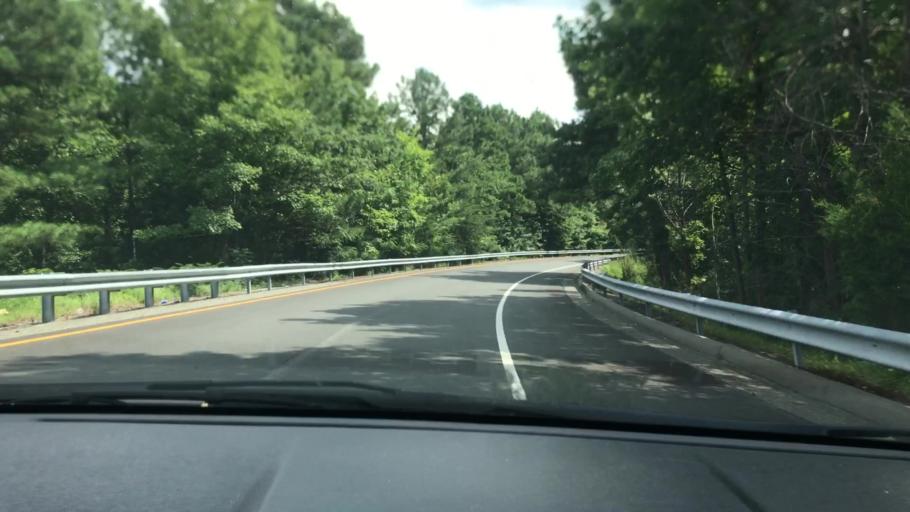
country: US
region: Virginia
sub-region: Henrico County
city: Short Pump
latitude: 37.6361
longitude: -77.5777
